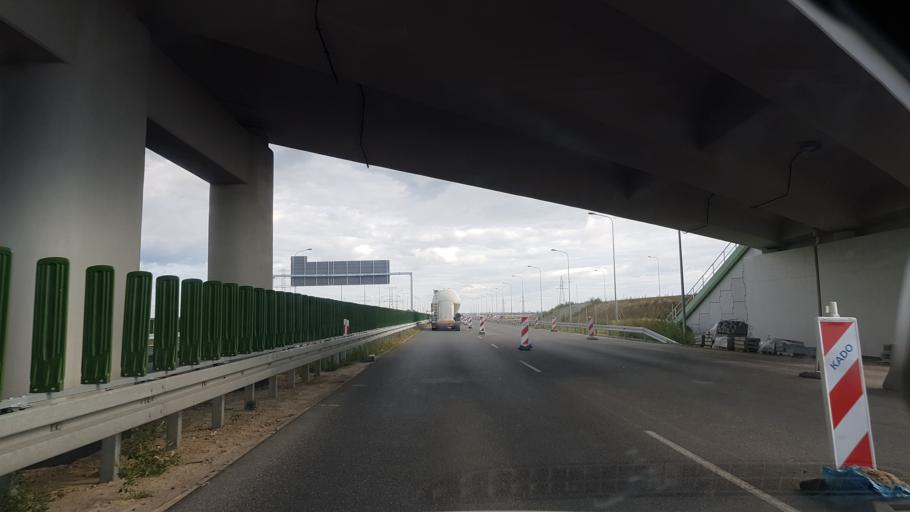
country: PL
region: Greater Poland Voivodeship
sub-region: Powiat poznanski
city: Steszew
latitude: 52.3334
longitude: 16.7325
